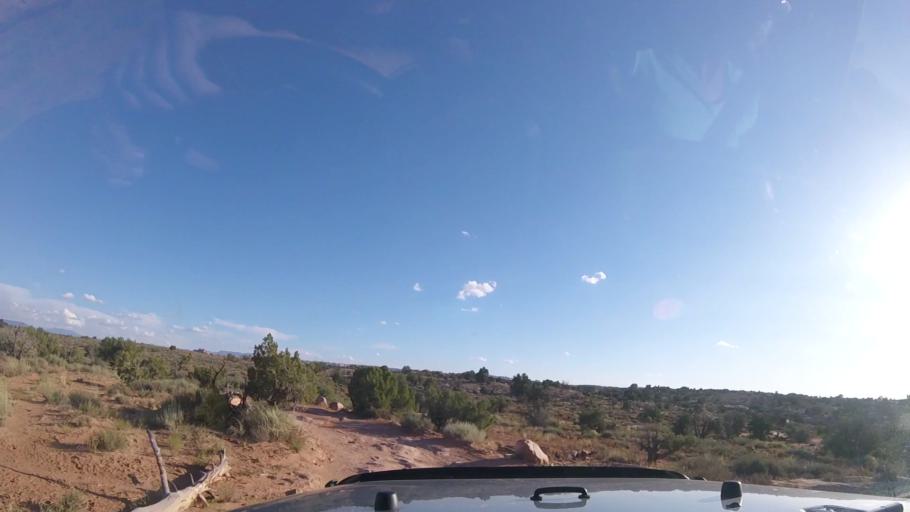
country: US
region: Utah
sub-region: Grand County
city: Moab
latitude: 38.2087
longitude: -109.7873
